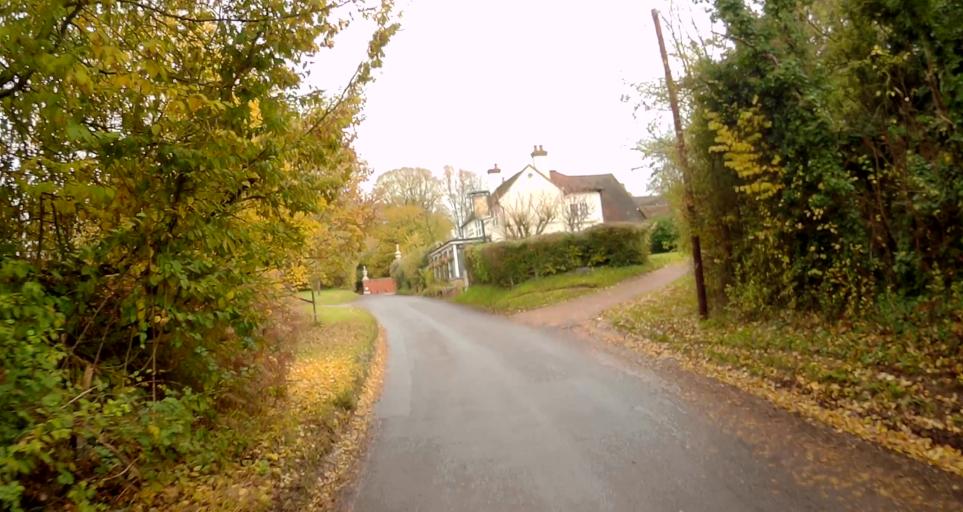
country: GB
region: England
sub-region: Hampshire
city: Long Sutton
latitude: 51.2182
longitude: -0.9309
